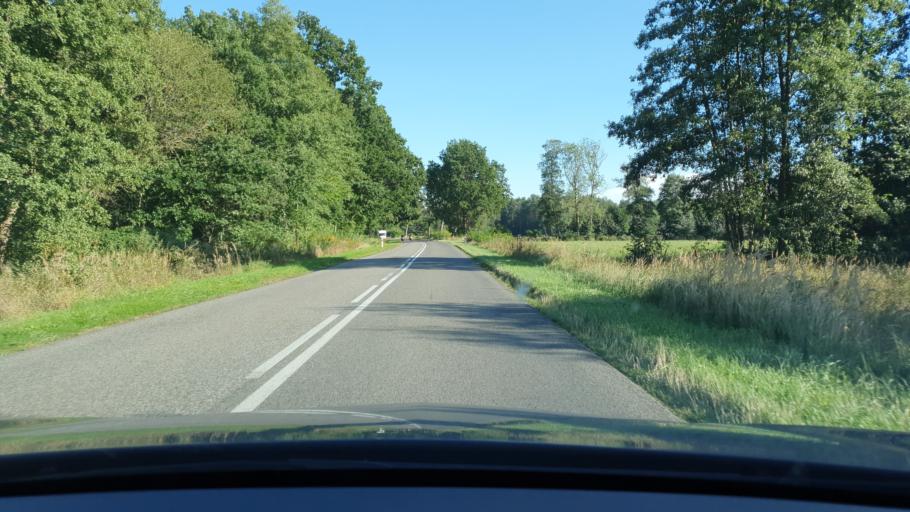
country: PL
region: West Pomeranian Voivodeship
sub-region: Powiat goleniowski
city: Przybiernow
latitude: 53.8292
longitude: 14.7777
